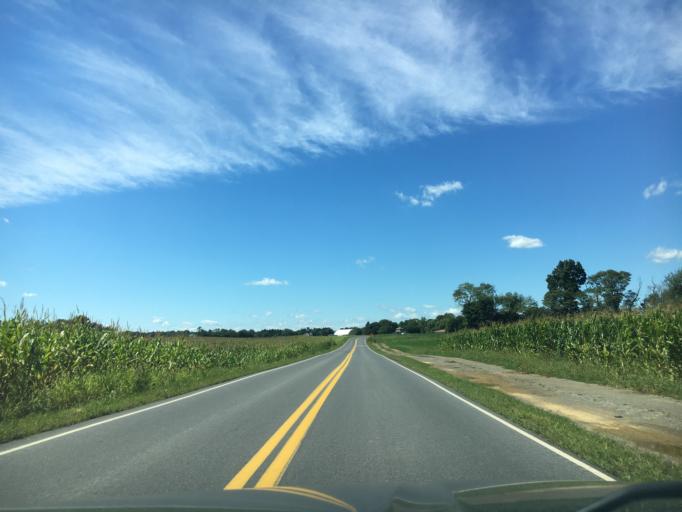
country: US
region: Pennsylvania
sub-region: Berks County
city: Topton
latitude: 40.5129
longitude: -75.6863
